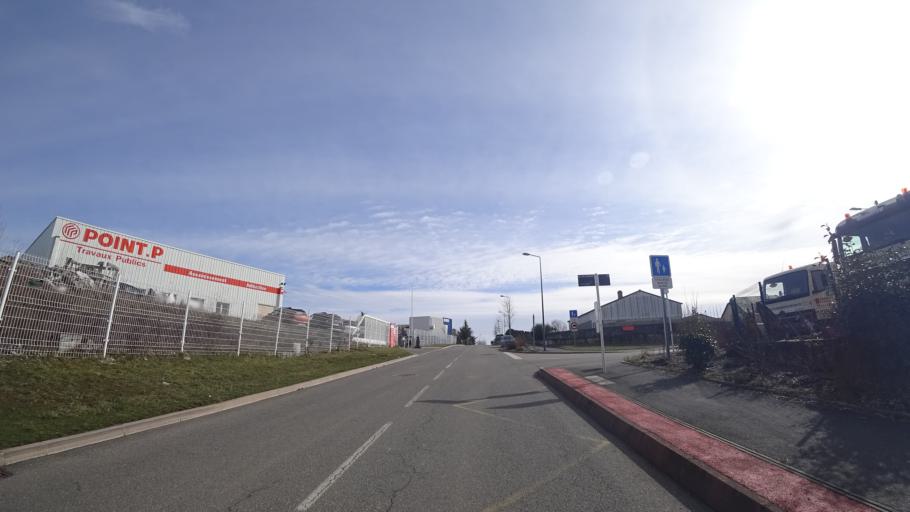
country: FR
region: Midi-Pyrenees
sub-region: Departement de l'Aveyron
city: Olemps
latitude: 44.3744
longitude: 2.5500
